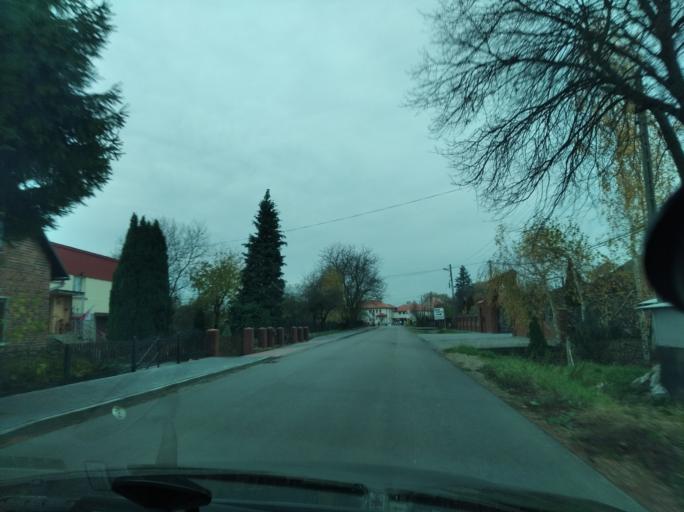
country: PL
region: Subcarpathian Voivodeship
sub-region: Powiat lancucki
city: Czarna
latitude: 50.0942
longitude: 22.1875
